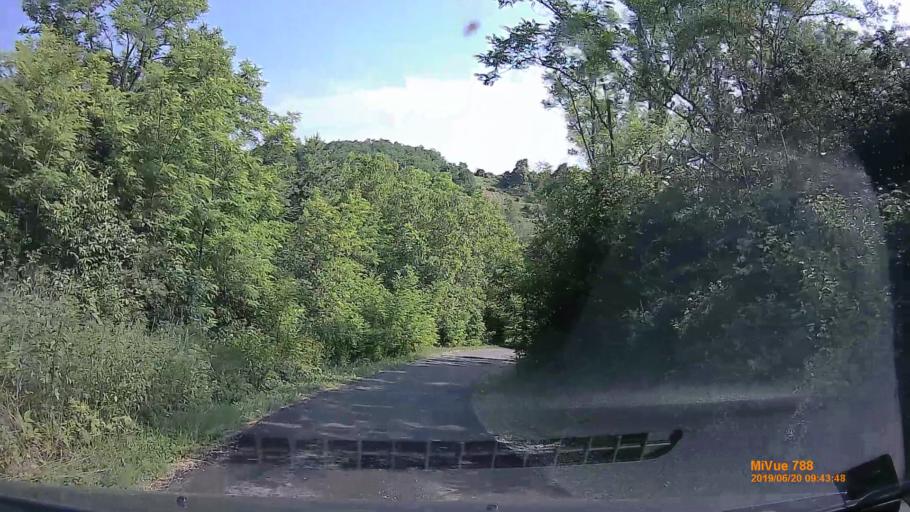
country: HU
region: Baranya
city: Pecsvarad
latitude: 46.1726
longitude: 18.4682
